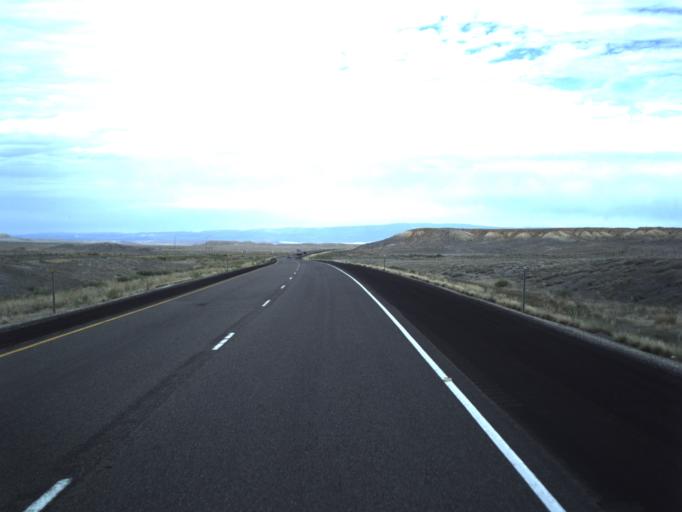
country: US
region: Utah
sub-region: Grand County
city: Moab
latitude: 38.9501
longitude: -109.6869
